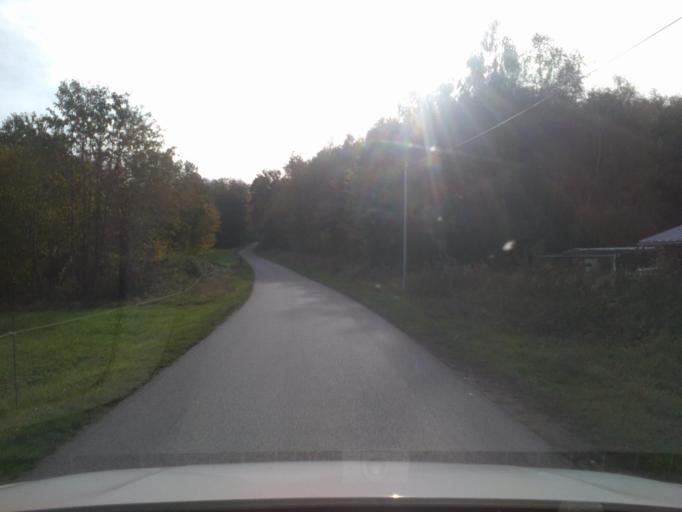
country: FR
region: Lorraine
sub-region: Departement des Vosges
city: Senones
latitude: 48.3847
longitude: 7.0041
